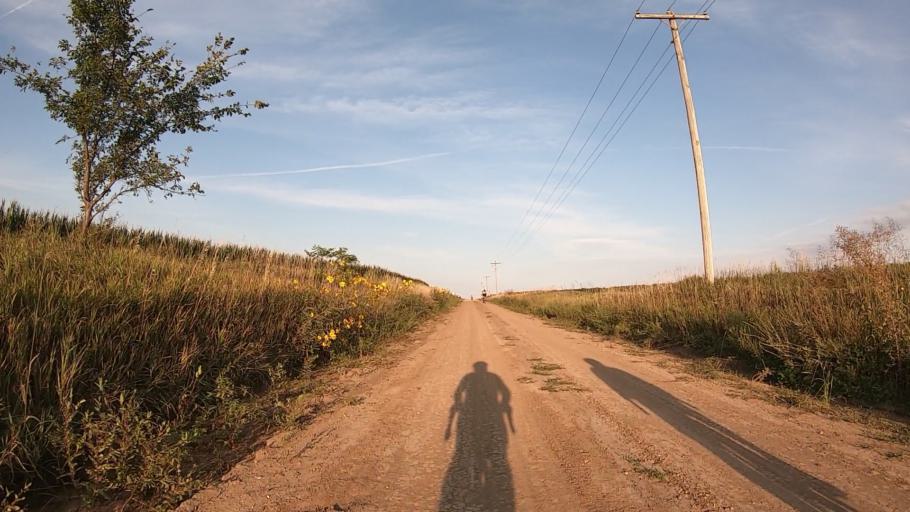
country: US
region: Kansas
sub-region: Marshall County
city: Marysville
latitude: 39.7694
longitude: -96.7306
